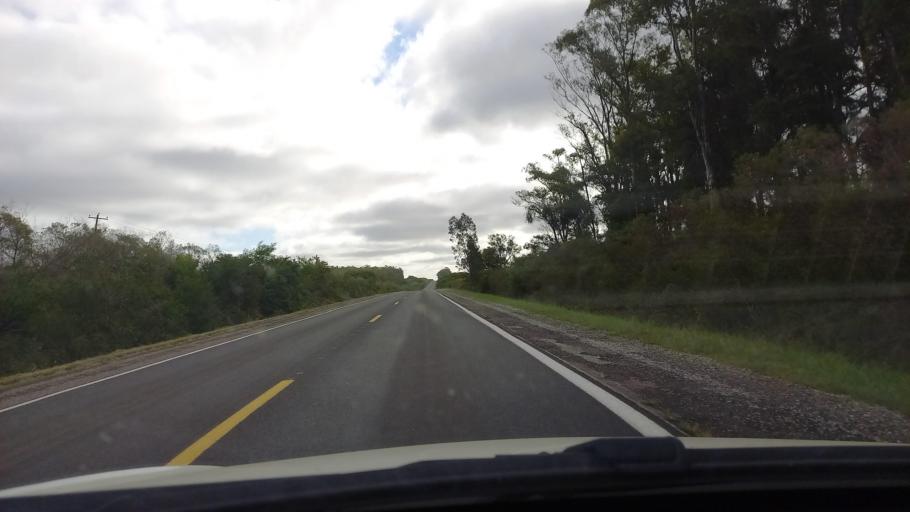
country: BR
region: Rio Grande do Sul
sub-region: Dom Pedrito
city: Dom Pedrito
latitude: -30.9145
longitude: -54.8004
